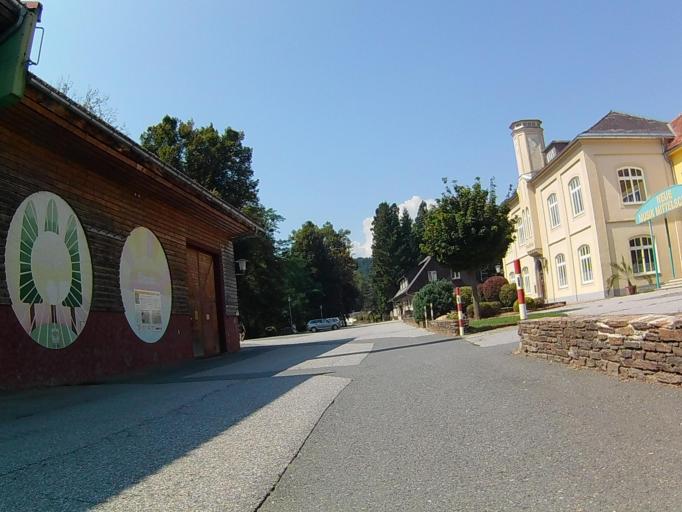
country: AT
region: Styria
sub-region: Politischer Bezirk Deutschlandsberg
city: Eibiswald
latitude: 46.6886
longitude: 15.2435
